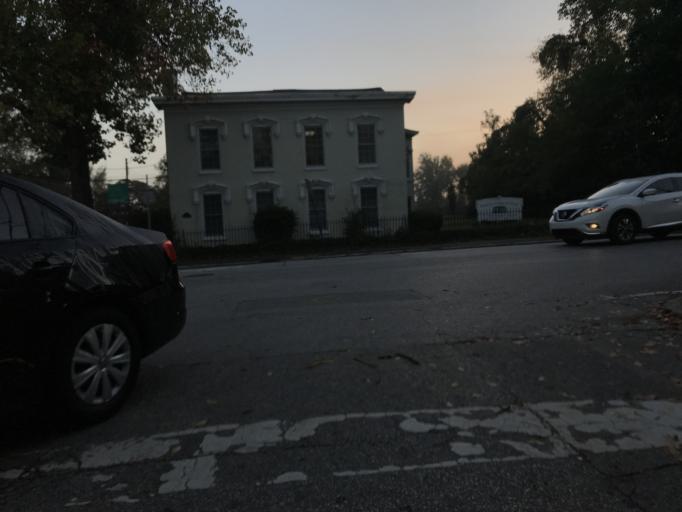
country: US
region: Indiana
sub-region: Clark County
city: Jeffersonville
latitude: 38.2581
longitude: -85.7259
